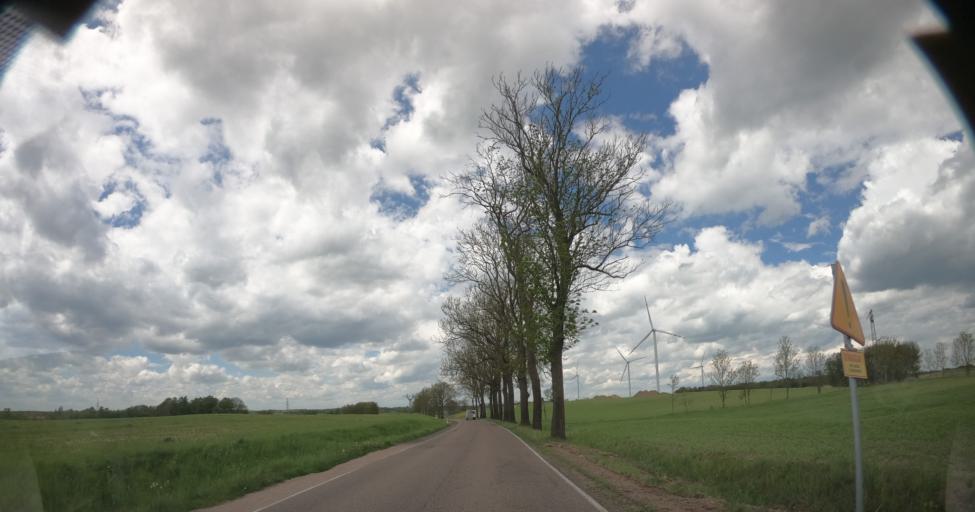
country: PL
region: West Pomeranian Voivodeship
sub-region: Powiat drawski
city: Drawsko Pomorskie
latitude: 53.5482
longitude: 15.7861
